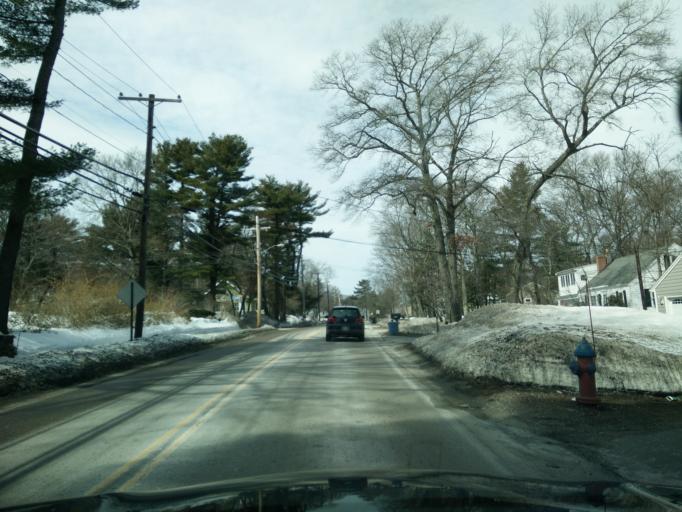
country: US
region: Massachusetts
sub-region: Norfolk County
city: Walpole
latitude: 42.1428
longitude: -71.2234
